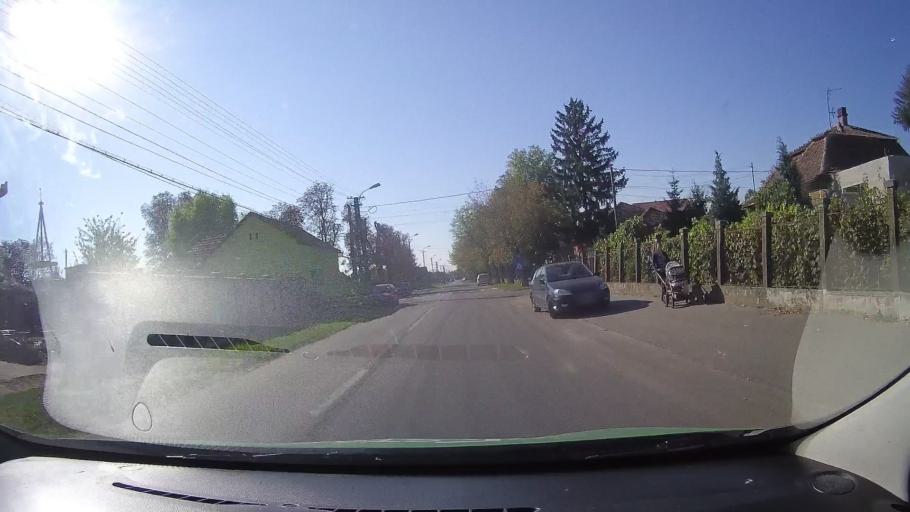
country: RO
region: Satu Mare
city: Carei
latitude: 47.6782
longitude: 22.4584
